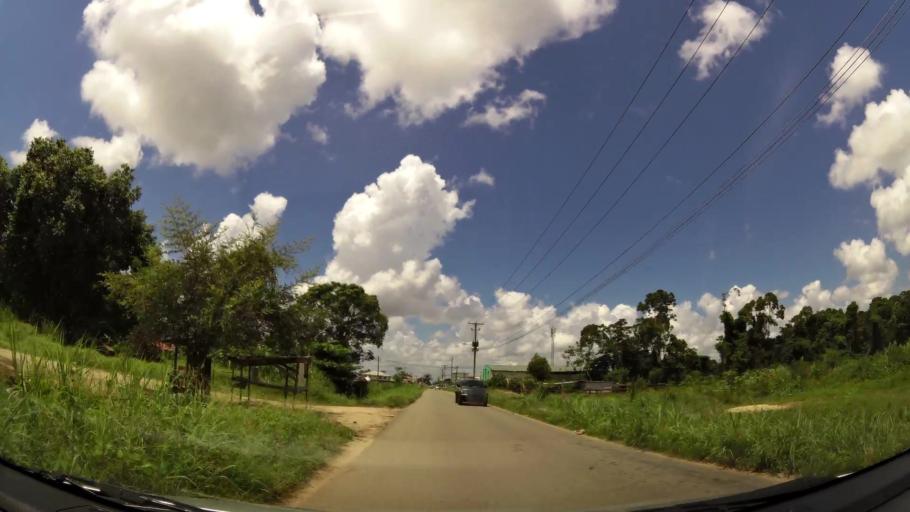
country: SR
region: Paramaribo
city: Paramaribo
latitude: 5.8586
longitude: -55.1665
